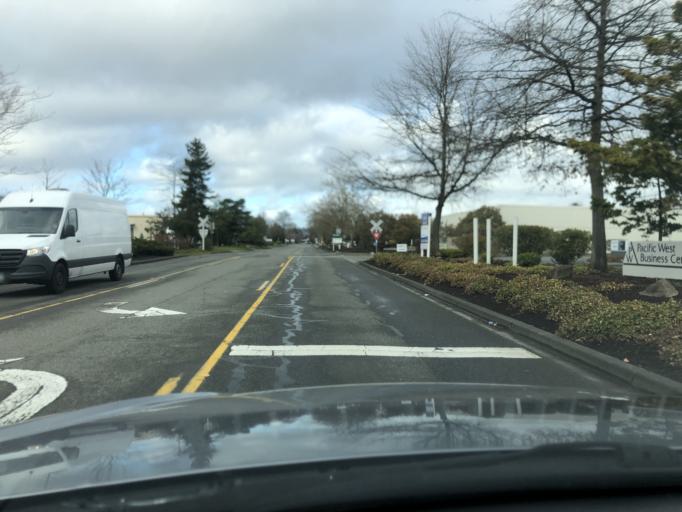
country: US
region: Washington
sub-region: King County
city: Tukwila
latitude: 47.4328
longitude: -122.2440
